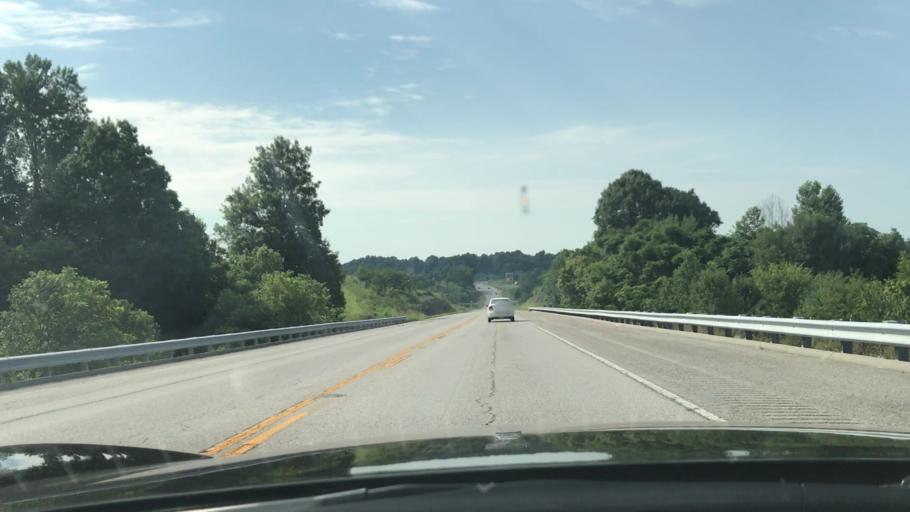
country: US
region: Kentucky
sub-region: Green County
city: Greensburg
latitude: 37.2811
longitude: -85.5149
